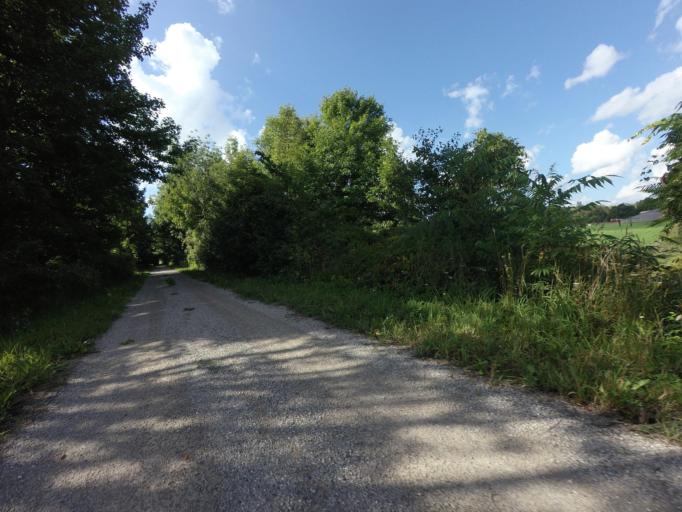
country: CA
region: Ontario
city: Goderich
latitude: 43.7490
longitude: -81.5005
